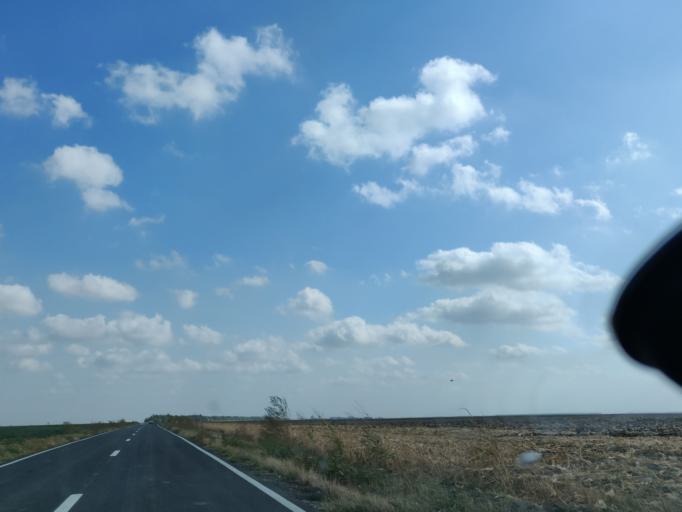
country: RO
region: Vrancea
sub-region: Comuna Ciorasti
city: Mihalceni
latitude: 45.4457
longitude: 27.3500
